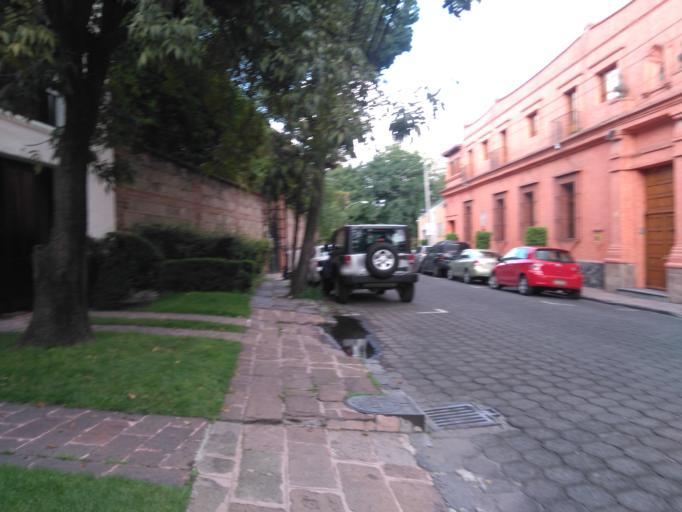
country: MX
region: Mexico City
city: Coyoacan
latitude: 19.3497
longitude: -99.1781
